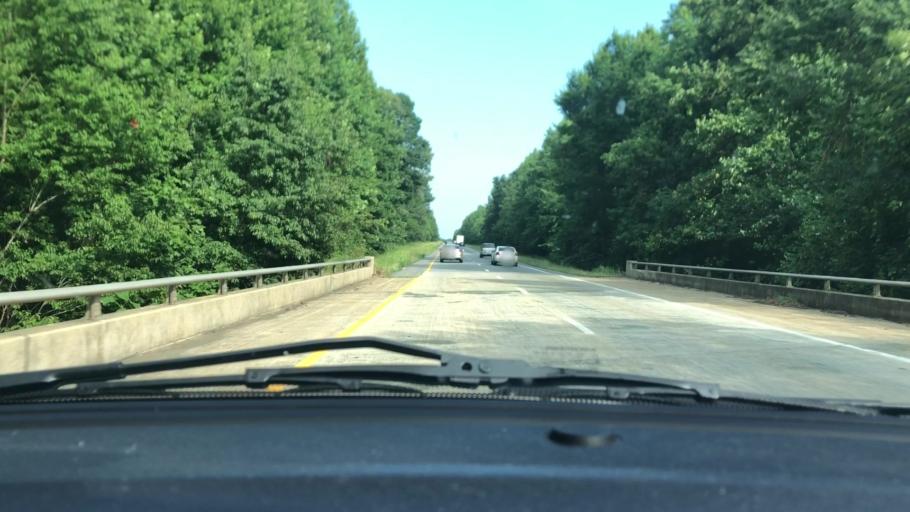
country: US
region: North Carolina
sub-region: Randolph County
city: Liberty
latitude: 35.8627
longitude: -79.6231
